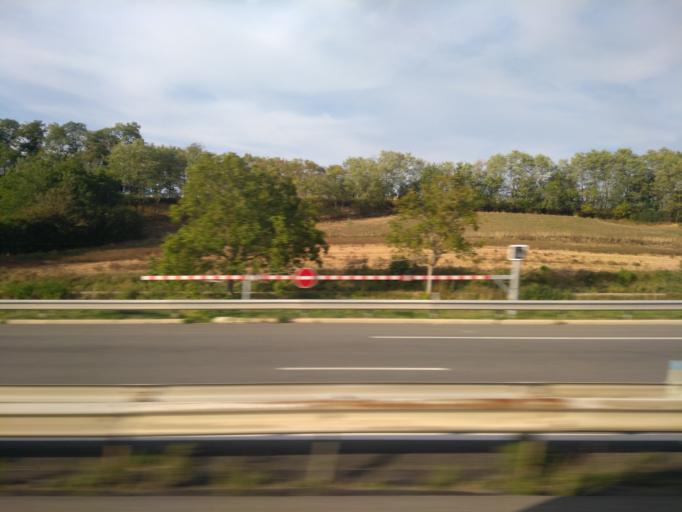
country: FR
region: Rhone-Alpes
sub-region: Departement de l'Isere
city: Cessieu
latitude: 45.5502
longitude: 5.3671
